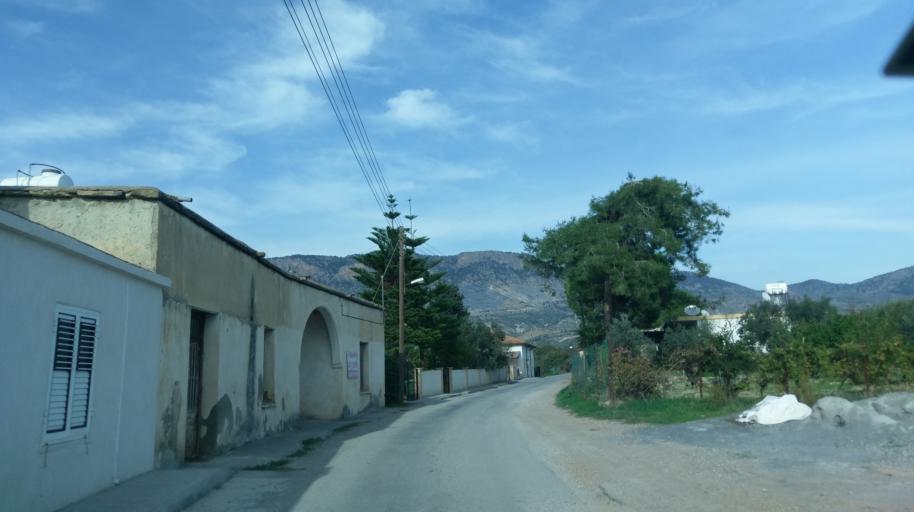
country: CY
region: Keryneia
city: Lapithos
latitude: 35.2796
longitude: 33.1731
